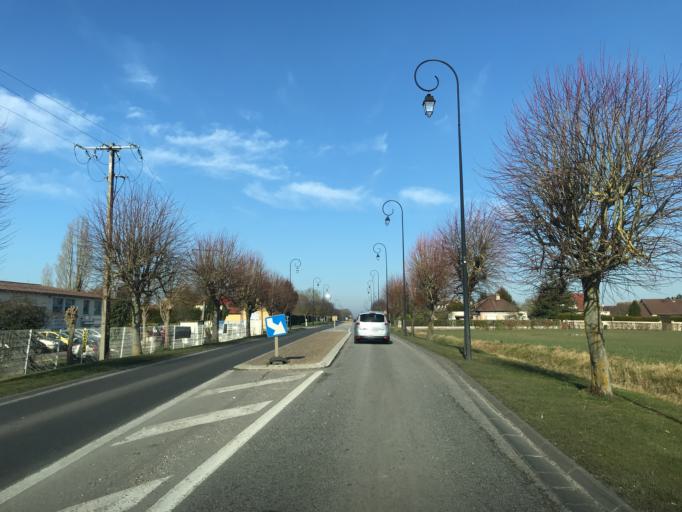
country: FR
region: Haute-Normandie
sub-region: Departement de l'Eure
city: Saint-Pierre-du-Vauvray
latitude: 49.2055
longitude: 1.2274
